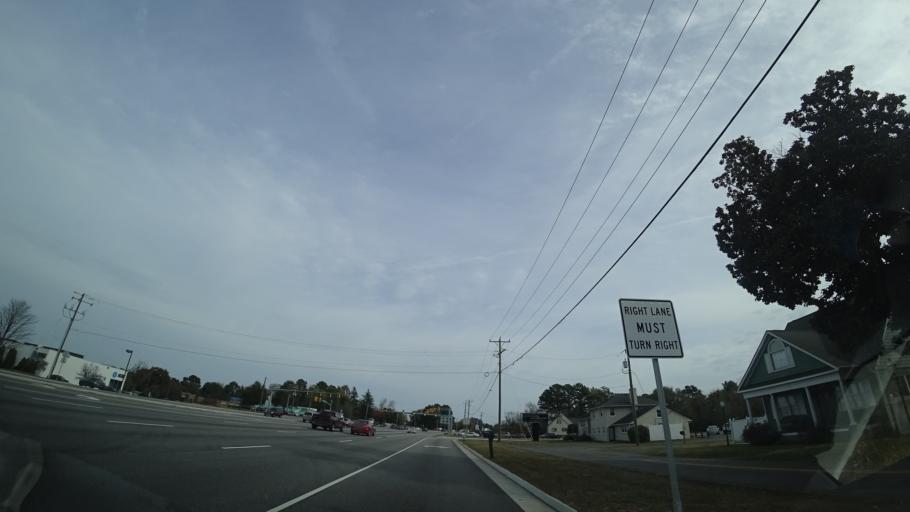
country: US
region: Virginia
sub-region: Hanover County
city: Mechanicsville
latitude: 37.6099
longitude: -77.3539
